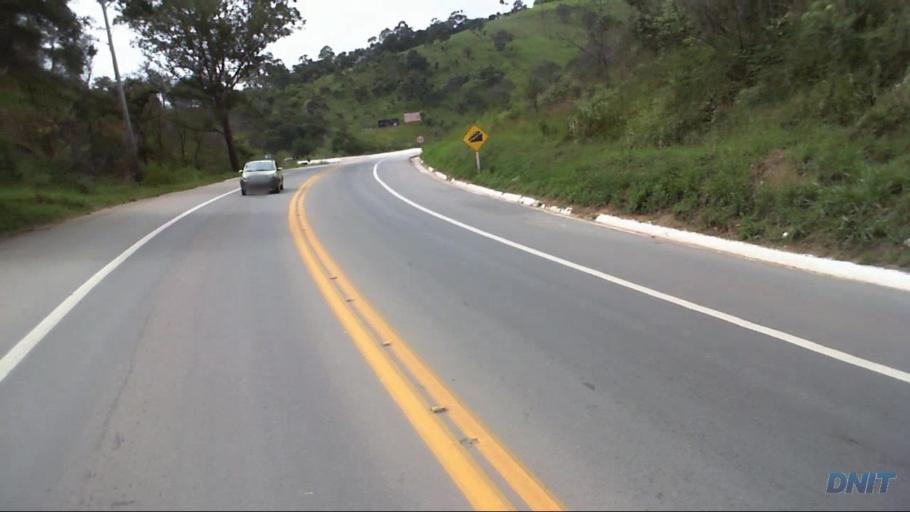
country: BR
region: Minas Gerais
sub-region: Caete
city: Caete
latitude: -19.7634
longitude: -43.6417
